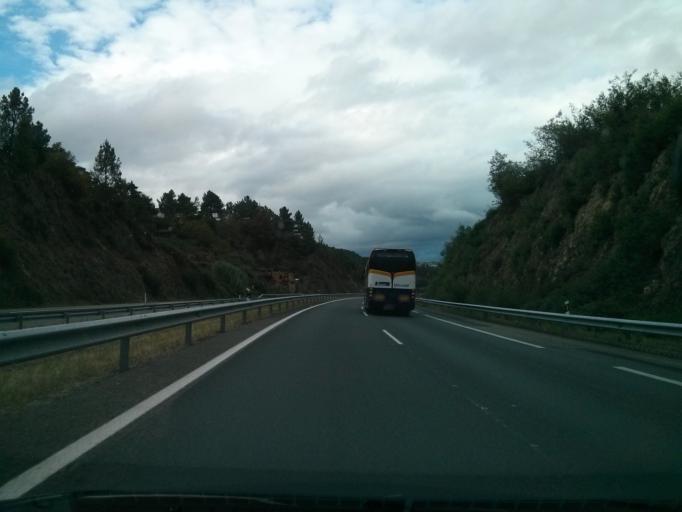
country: ES
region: Galicia
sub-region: Provincia de Ourense
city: Ourense
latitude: 42.3244
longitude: -7.8875
